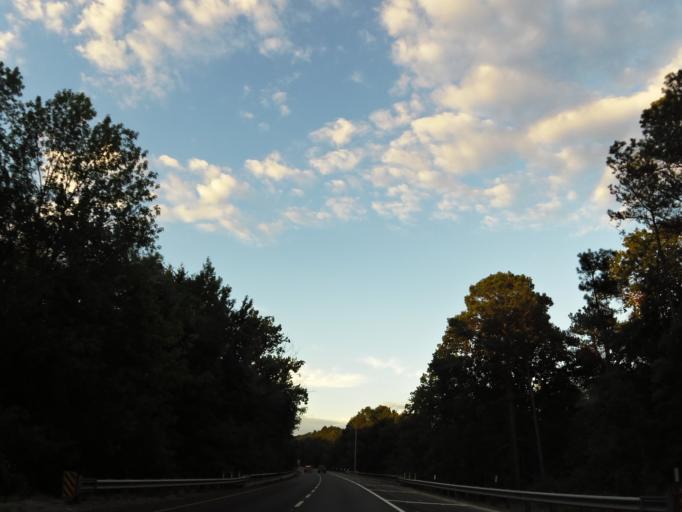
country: US
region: Tennessee
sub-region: Bradley County
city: Hopewell
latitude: 35.3319
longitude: -84.7570
